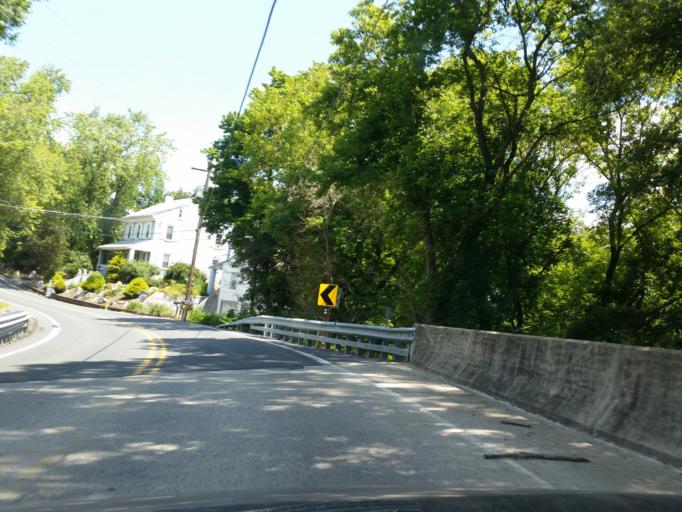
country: US
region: Pennsylvania
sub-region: Lebanon County
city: Annville
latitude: 40.3662
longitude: -76.5108
